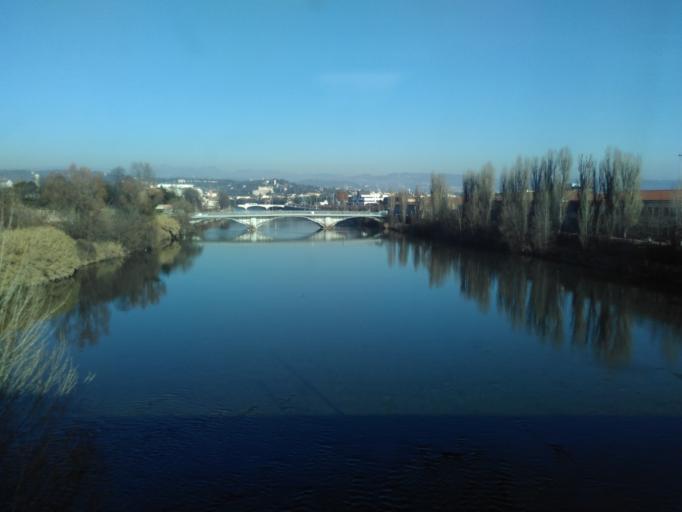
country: IT
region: Veneto
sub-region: Provincia di Verona
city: Verona
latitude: 45.4274
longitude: 10.9949
